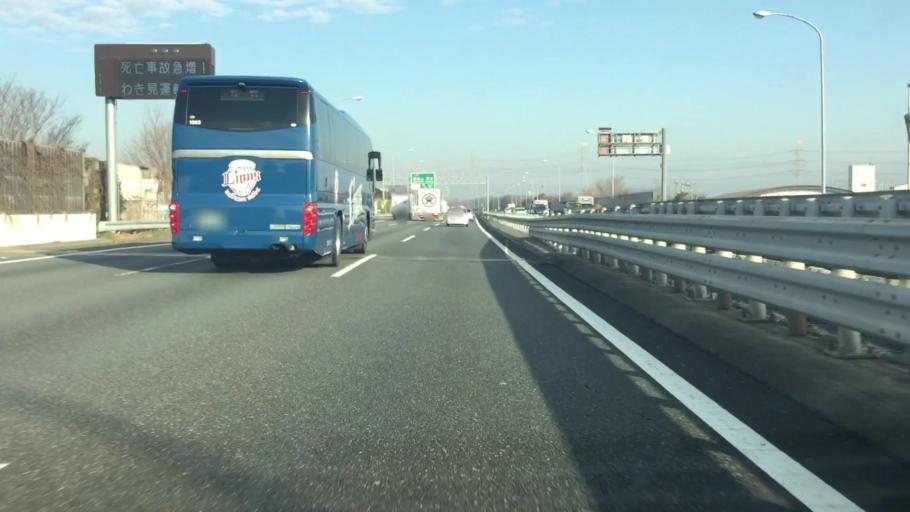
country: JP
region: Saitama
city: Sakado
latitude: 36.0211
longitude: 139.3823
